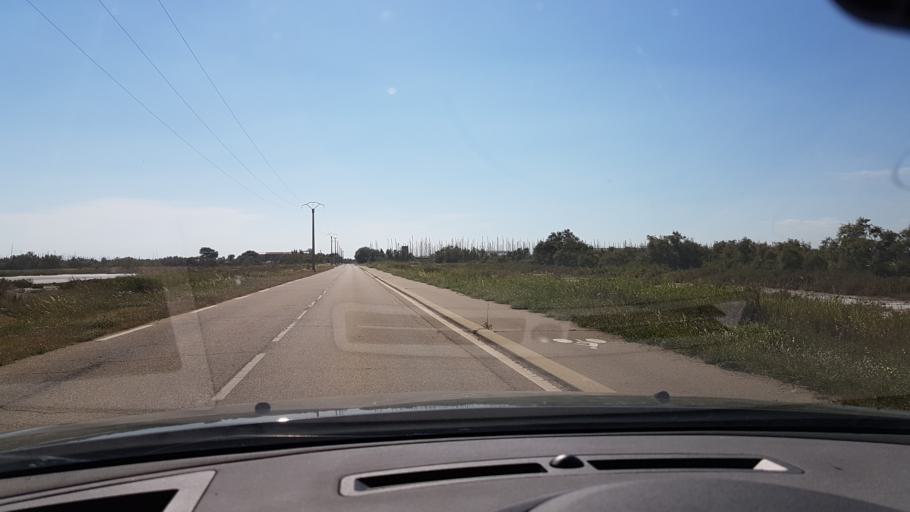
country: FR
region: Provence-Alpes-Cote d'Azur
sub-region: Departement des Bouches-du-Rhone
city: Port-Saint-Louis-du-Rhone
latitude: 43.3827
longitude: 4.8464
